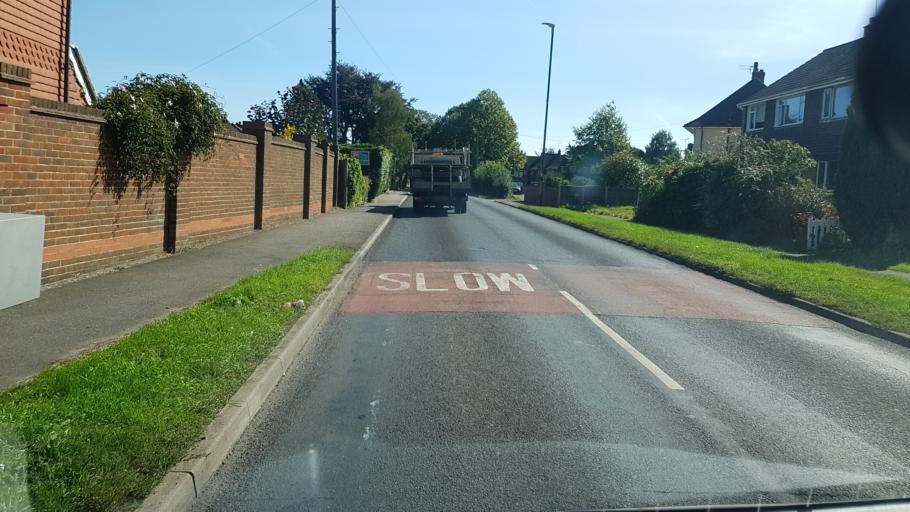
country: GB
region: England
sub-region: Kent
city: Maidstone
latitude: 51.2343
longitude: 0.4891
